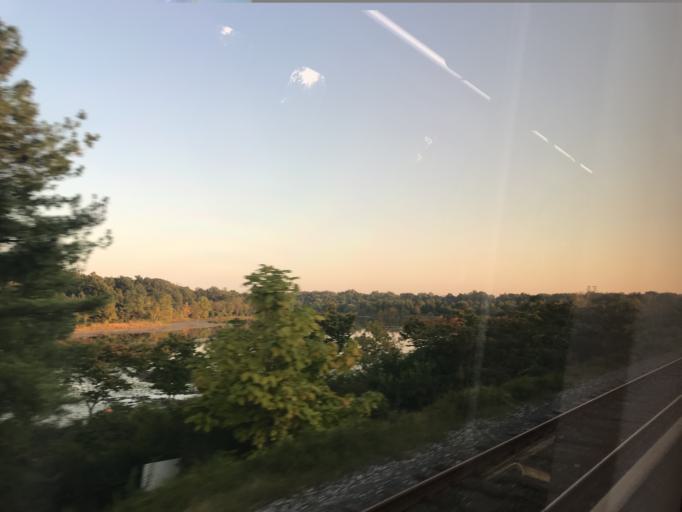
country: US
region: Maryland
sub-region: Prince George's County
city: Berwyn Heights
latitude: 38.9908
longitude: -76.9232
